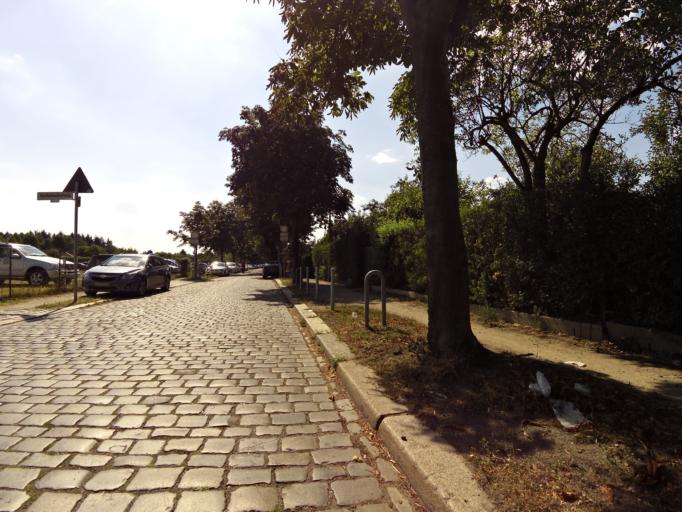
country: DE
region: Berlin
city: Schoneberg Bezirk
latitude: 52.4710
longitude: 13.3560
